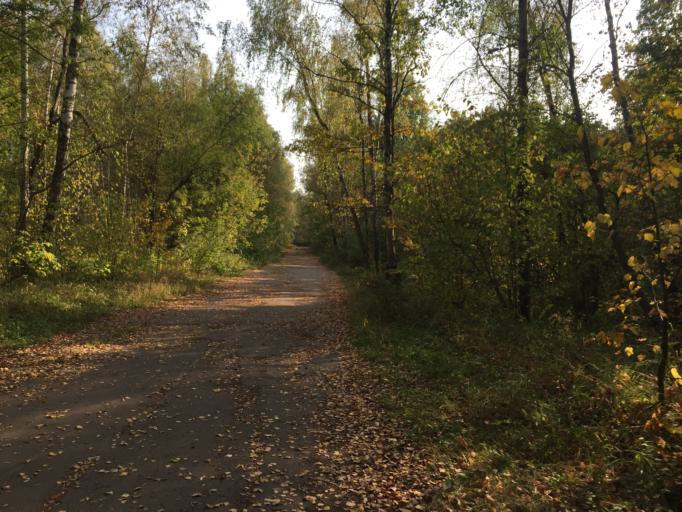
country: RU
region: Moscow
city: Babushkin
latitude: 55.8485
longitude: 37.7195
